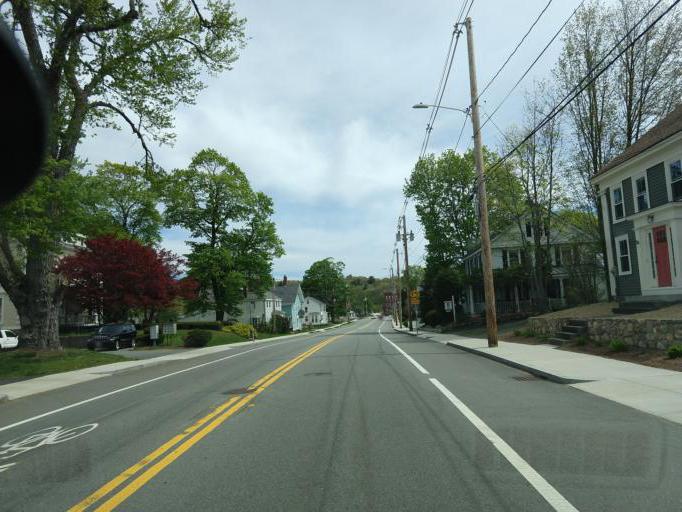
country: US
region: Massachusetts
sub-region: Essex County
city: Merrimac
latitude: 42.8318
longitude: -71.0048
